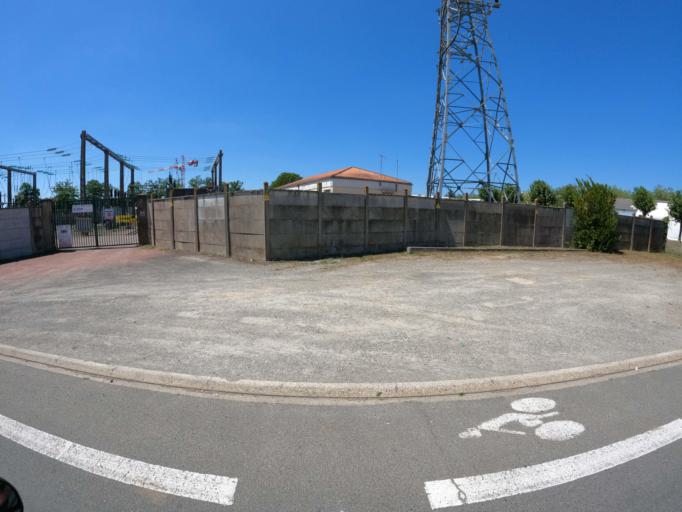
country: FR
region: Pays de la Loire
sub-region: Departement de la Vendee
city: Challans
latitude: 46.8494
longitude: -1.8594
